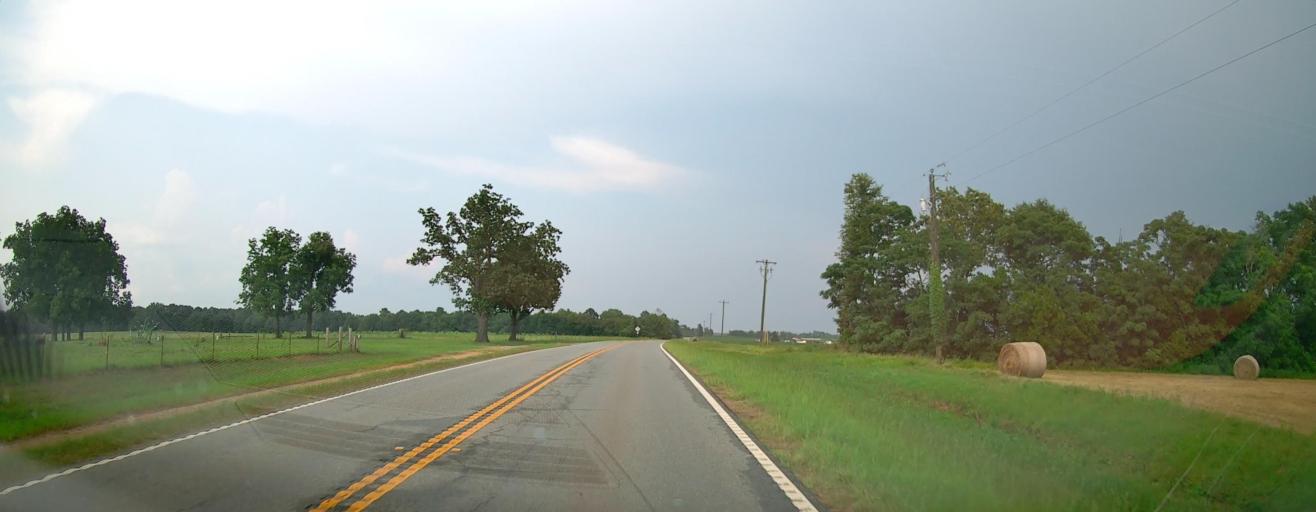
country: US
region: Georgia
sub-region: Twiggs County
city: Jeffersonville
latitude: 32.5798
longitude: -83.3920
